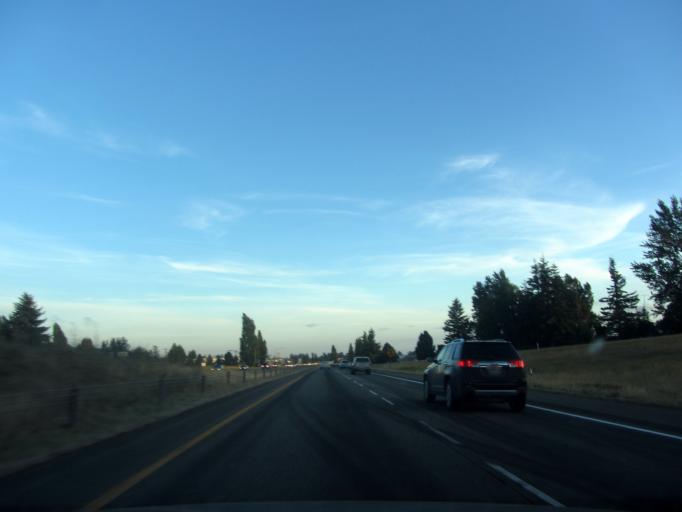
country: US
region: Washington
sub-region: Skagit County
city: Mount Vernon
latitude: 48.3993
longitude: -122.3306
